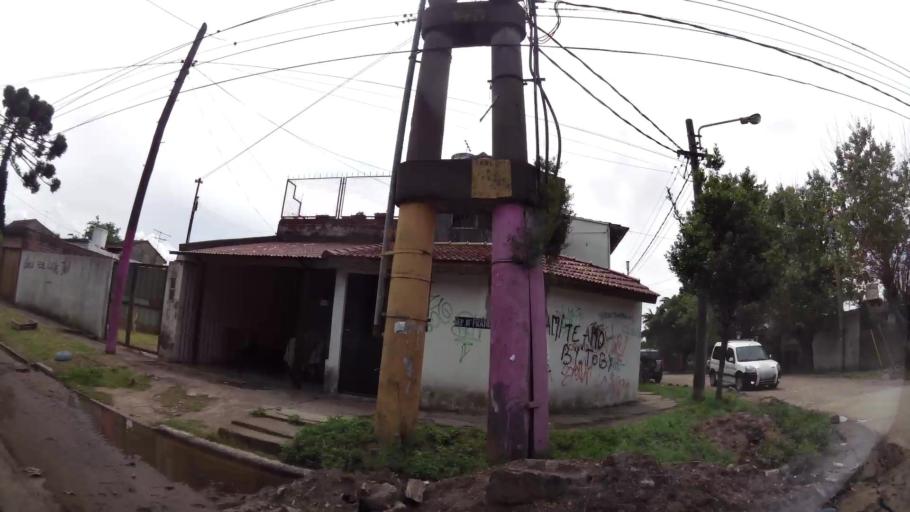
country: AR
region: Buenos Aires
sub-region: Partido de Quilmes
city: Quilmes
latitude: -34.7717
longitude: -58.2768
